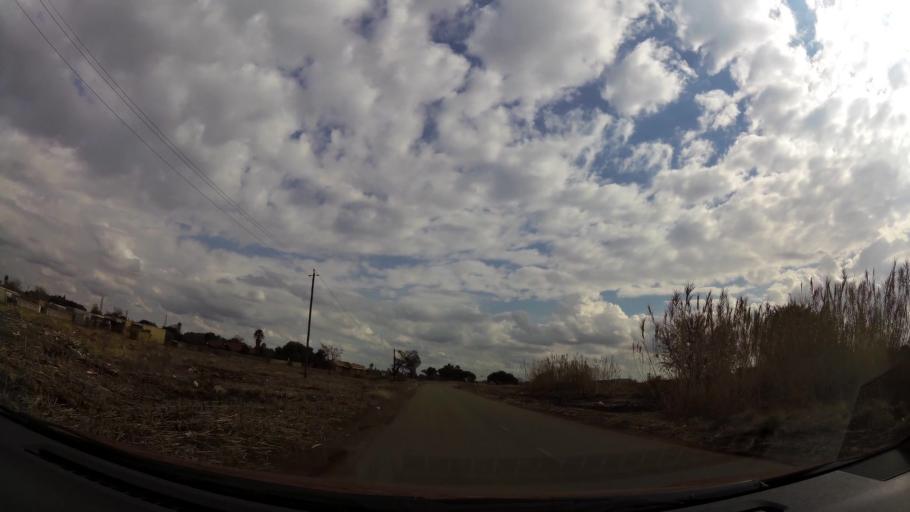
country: ZA
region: Gauteng
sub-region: Sedibeng District Municipality
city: Vanderbijlpark
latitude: -26.7002
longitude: 27.7945
